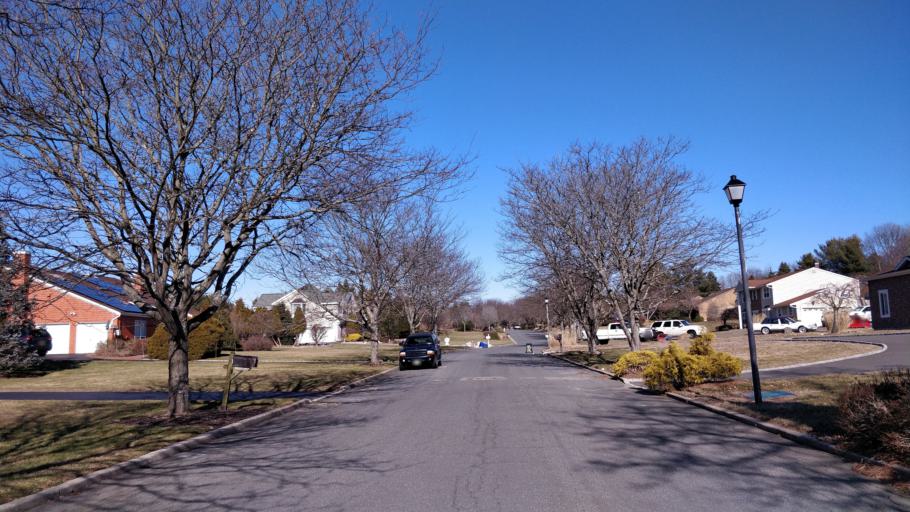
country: US
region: New York
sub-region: Suffolk County
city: Saint James
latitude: 40.8895
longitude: -73.1382
